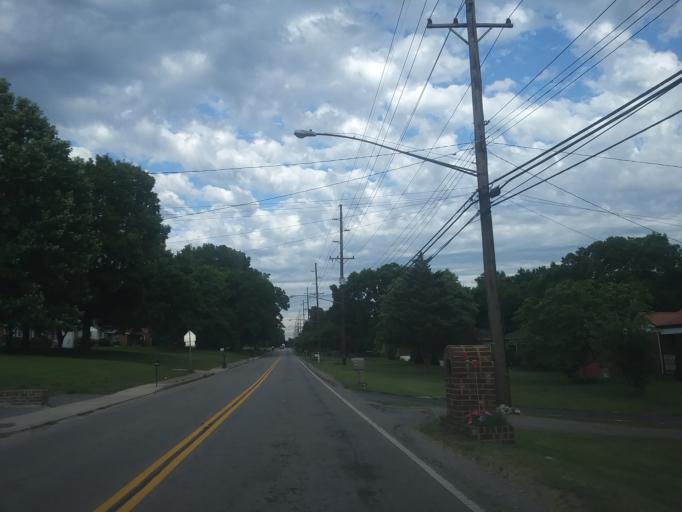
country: US
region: Tennessee
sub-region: Davidson County
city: Oak Hill
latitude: 36.0988
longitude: -86.7314
